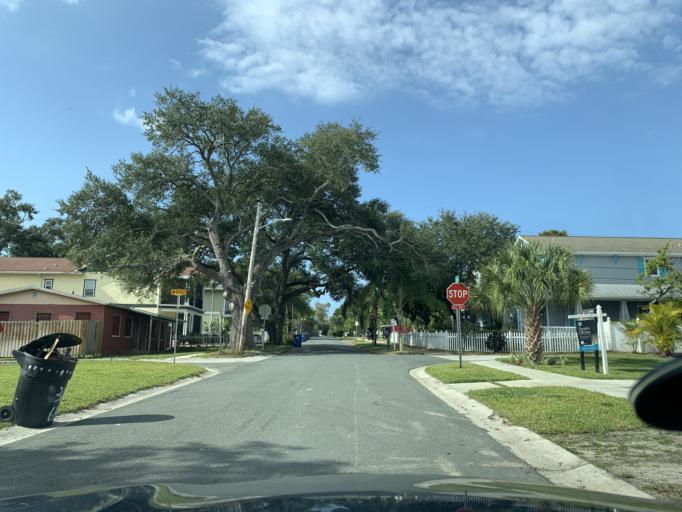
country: US
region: Florida
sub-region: Pinellas County
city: Saint Petersburg
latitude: 27.7585
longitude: -82.6417
